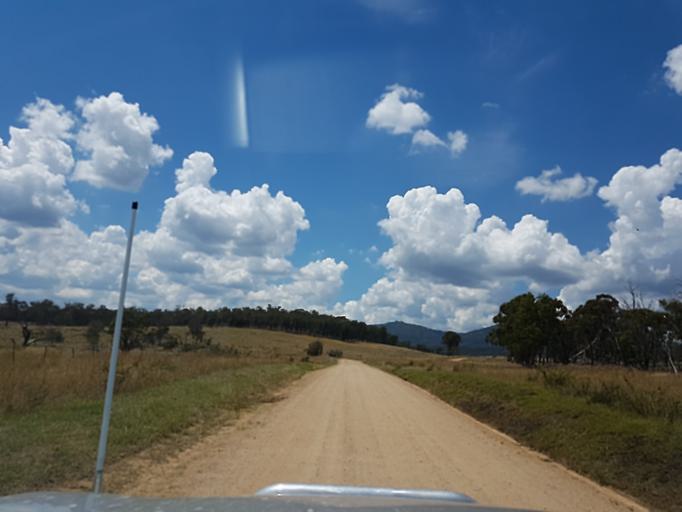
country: AU
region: Victoria
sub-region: Alpine
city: Mount Beauty
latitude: -36.8988
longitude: 147.8468
